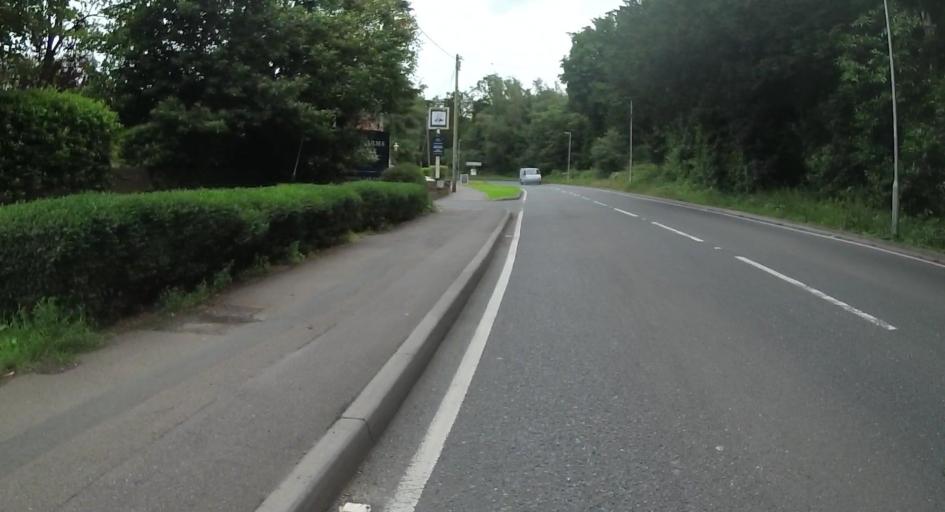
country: GB
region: England
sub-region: Wokingham
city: Winnersh
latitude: 51.4186
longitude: -0.8829
